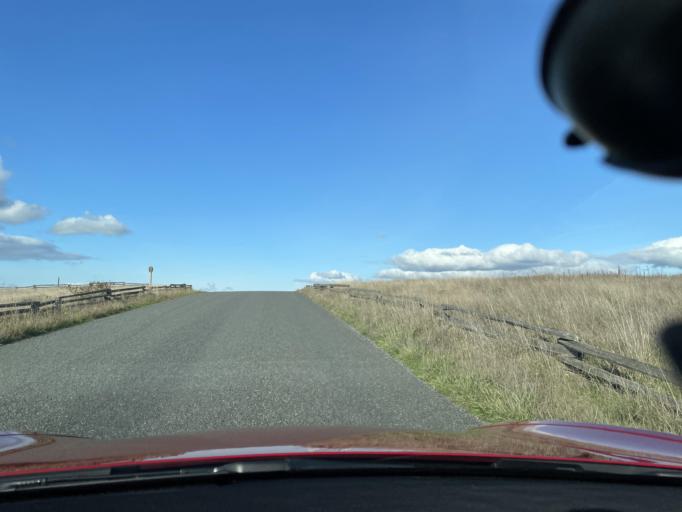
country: US
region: Washington
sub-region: San Juan County
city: Friday Harbor
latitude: 48.4620
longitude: -123.0015
